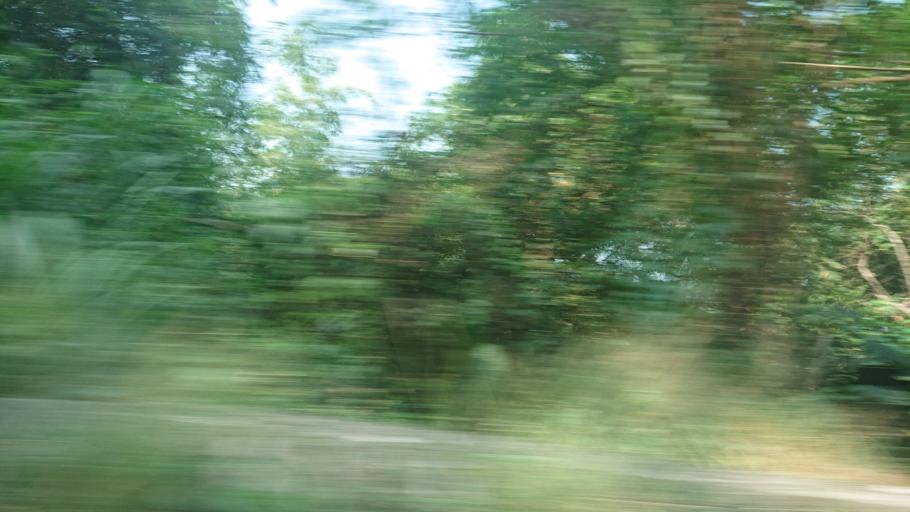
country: TW
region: Taiwan
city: Lugu
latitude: 23.7063
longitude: 120.6635
